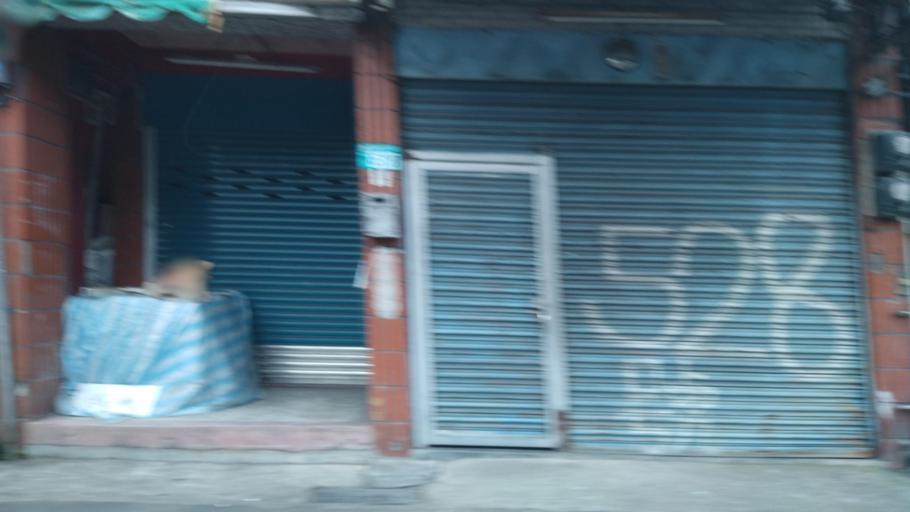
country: TW
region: Taipei
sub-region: Taipei
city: Banqiao
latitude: 24.9494
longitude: 121.4827
